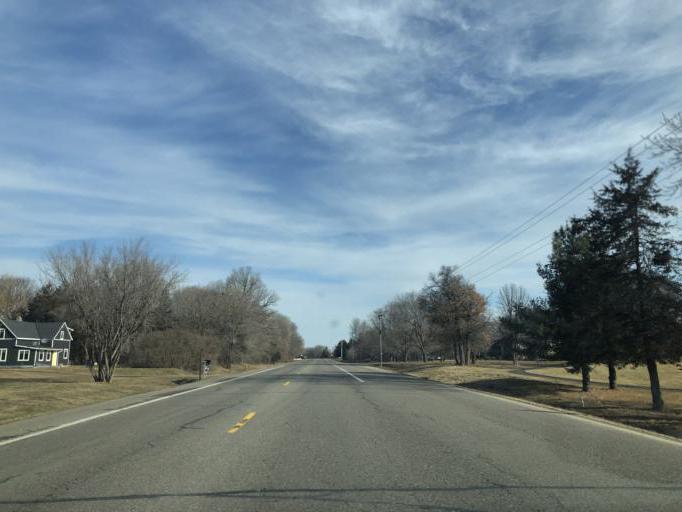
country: US
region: Minnesota
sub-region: Sherburne County
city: Becker
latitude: 45.4143
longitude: -93.8709
